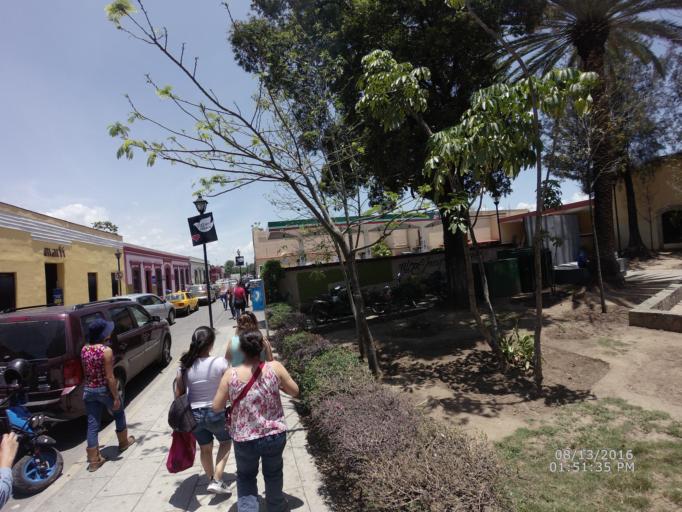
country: MX
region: Oaxaca
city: Oaxaca de Juarez
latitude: 17.0614
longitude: -96.7224
